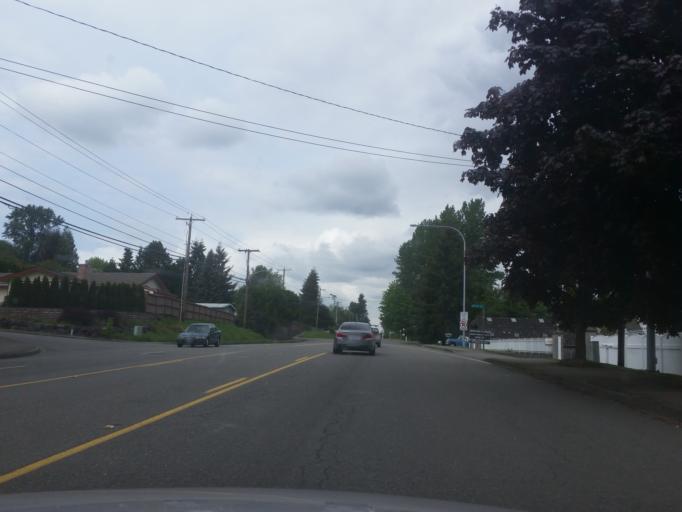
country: US
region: Washington
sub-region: King County
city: Inglewood-Finn Hill
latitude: 47.7249
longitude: -122.2077
